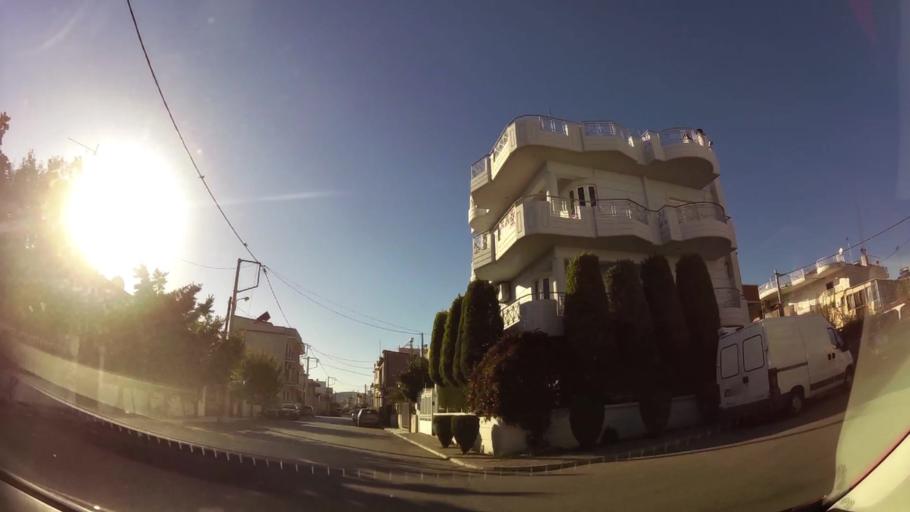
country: GR
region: Attica
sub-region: Nomarchia Anatolikis Attikis
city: Acharnes
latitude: 38.0875
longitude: 23.7283
